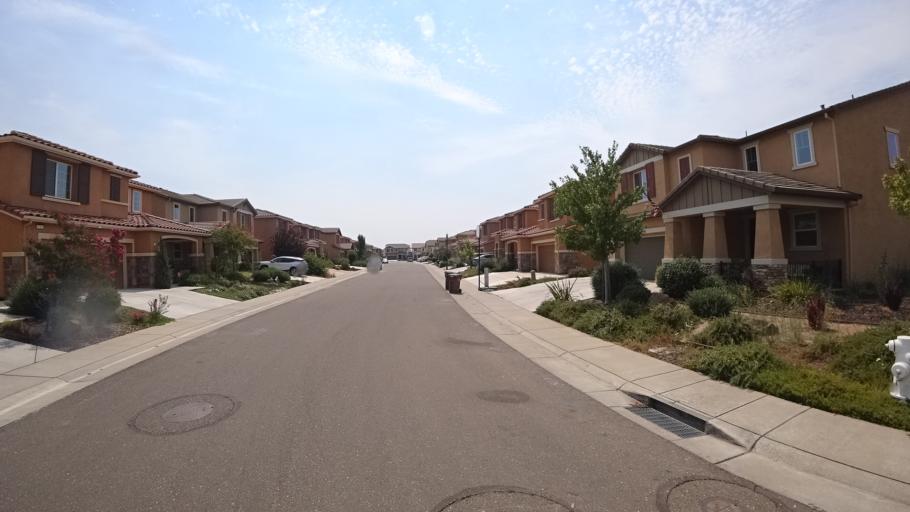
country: US
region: California
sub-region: Sacramento County
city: Laguna
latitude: 38.4056
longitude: -121.4064
